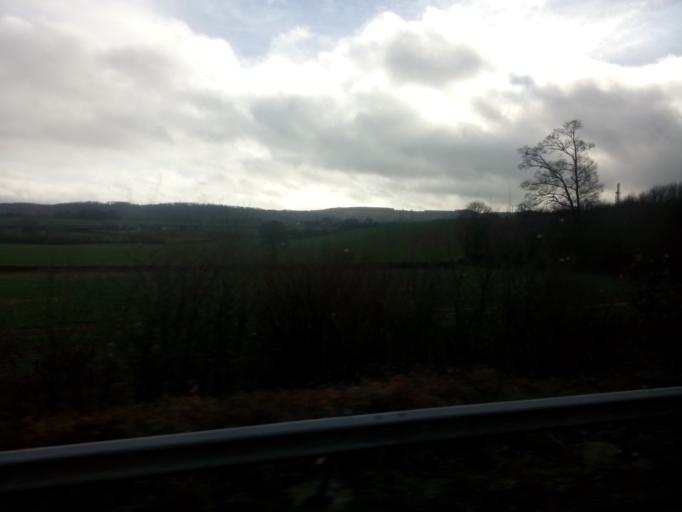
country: GB
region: England
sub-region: Somerset
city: Taunton
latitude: 50.9869
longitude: -3.1055
